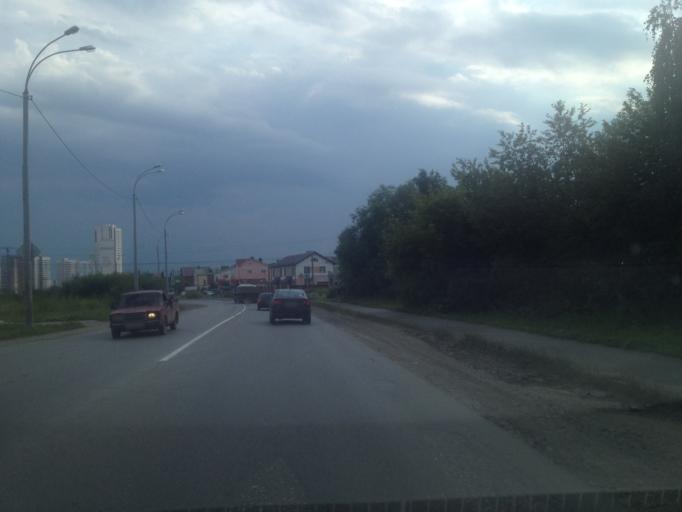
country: RU
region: Sverdlovsk
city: Shirokaya Rechka
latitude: 56.8061
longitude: 60.4954
